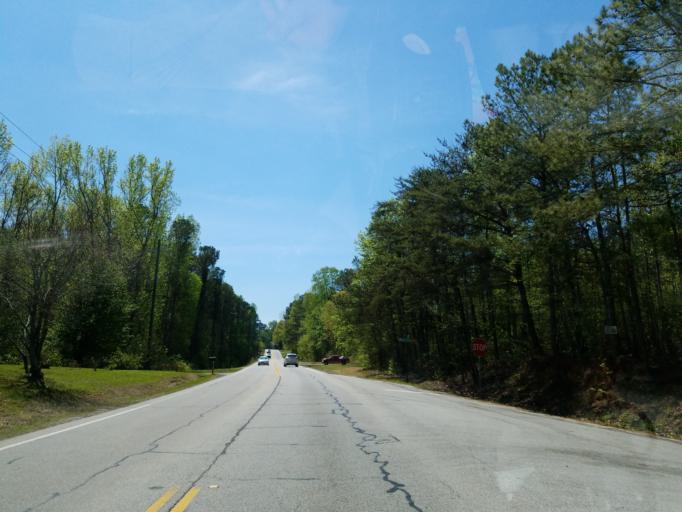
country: US
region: Georgia
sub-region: Paulding County
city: Hiram
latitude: 33.8680
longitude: -84.7862
